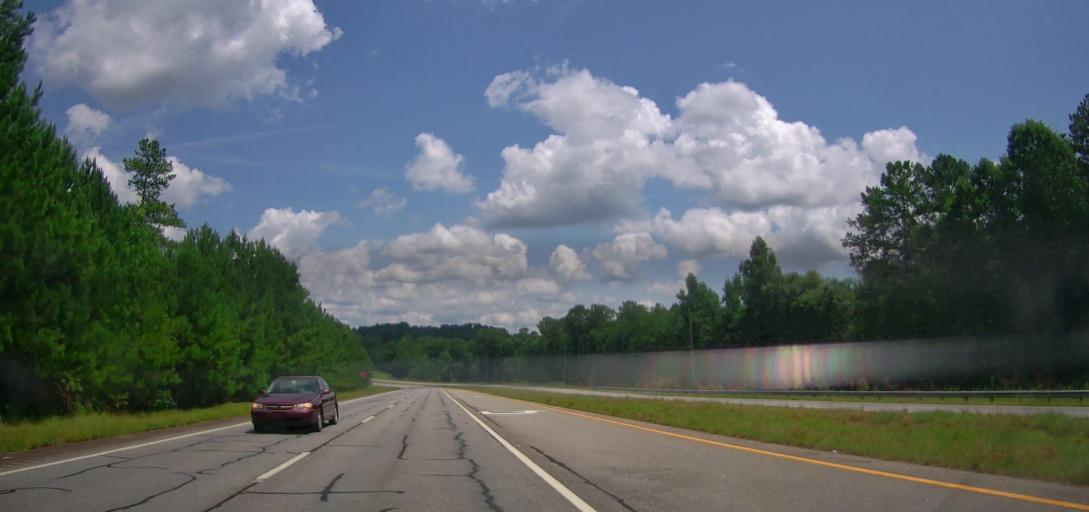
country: US
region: Georgia
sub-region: Heard County
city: Franklin
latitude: 33.2605
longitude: -85.0659
